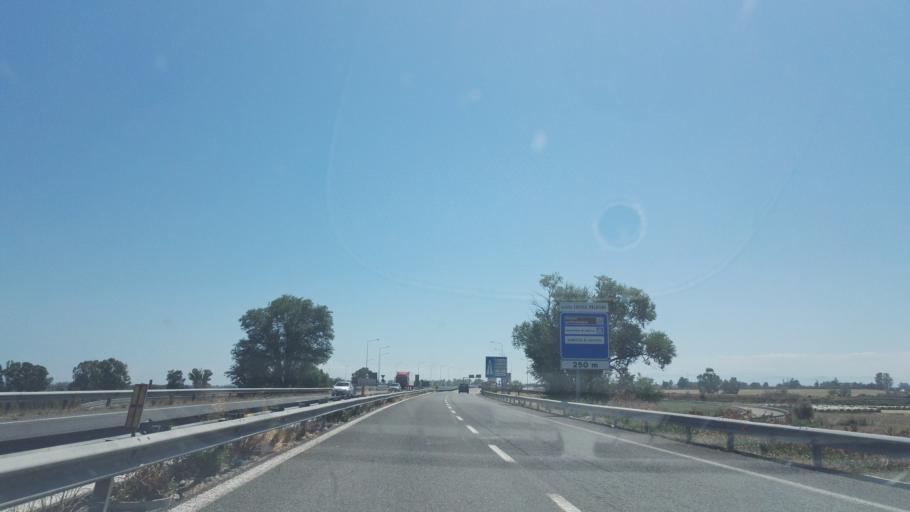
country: IT
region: Apulia
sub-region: Provincia di Taranto
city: Marina di Ginosa
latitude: 40.4214
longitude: 16.8243
